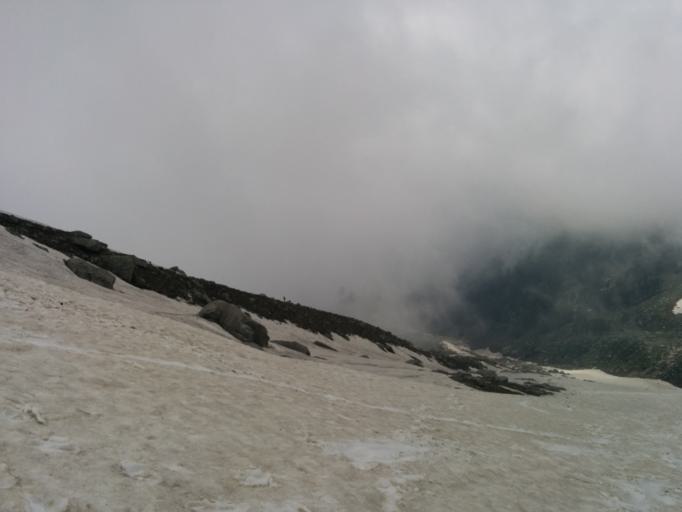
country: IN
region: Himachal Pradesh
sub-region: Kangra
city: Dharmsala
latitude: 32.2848
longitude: 76.3683
